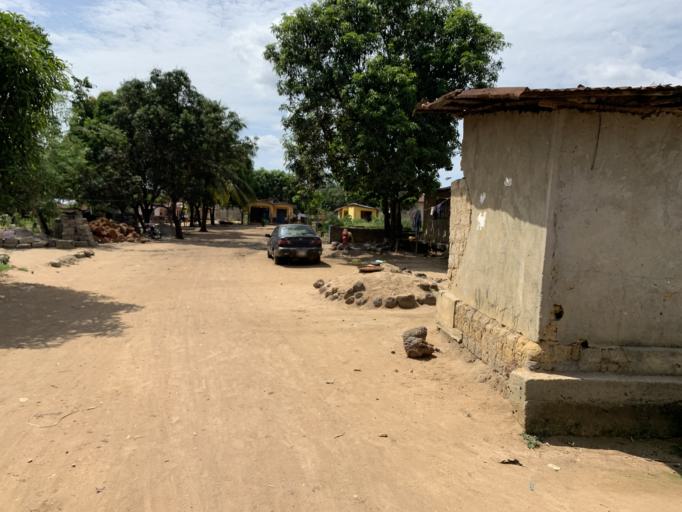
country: SL
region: Western Area
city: Waterloo
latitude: 8.3303
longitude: -13.0462
